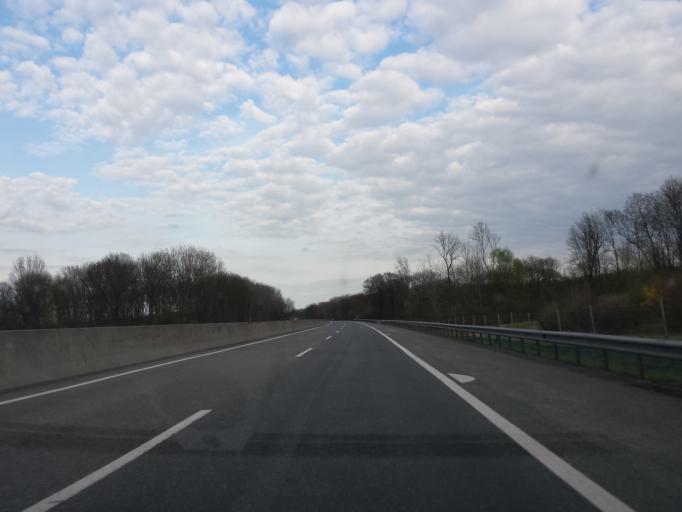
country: AT
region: Lower Austria
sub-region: Politischer Bezirk Korneuburg
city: Stetteldorf am Wagram
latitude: 48.3576
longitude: 16.0056
